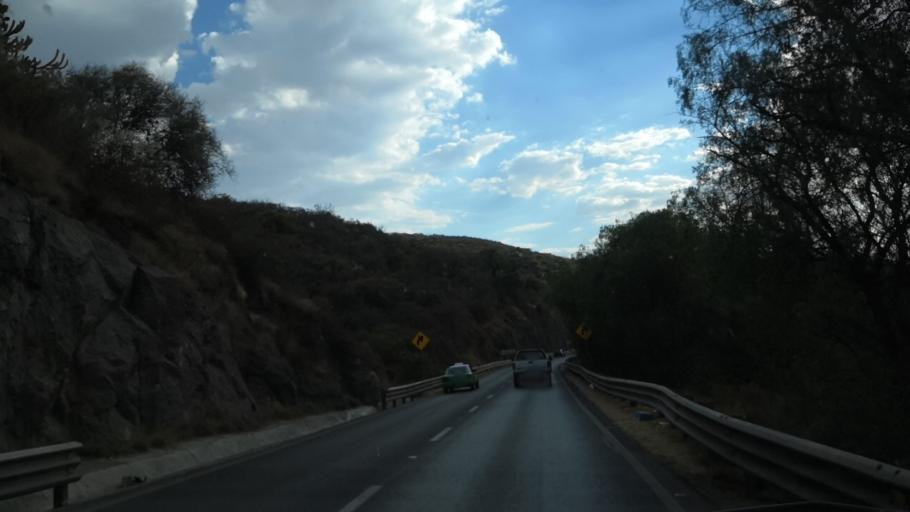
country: MX
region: Guanajuato
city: Marfil
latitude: 21.0059
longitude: -101.2747
